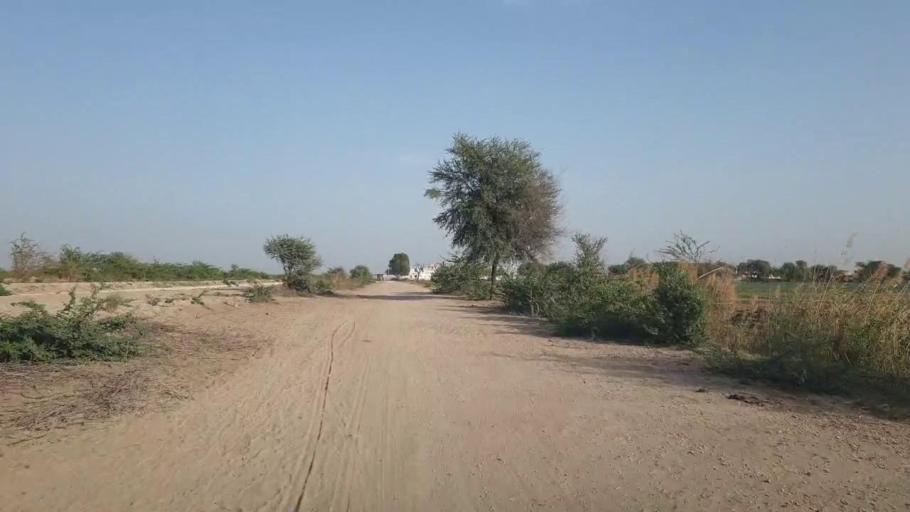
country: PK
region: Sindh
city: Dhoro Naro
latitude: 25.4850
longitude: 69.5824
